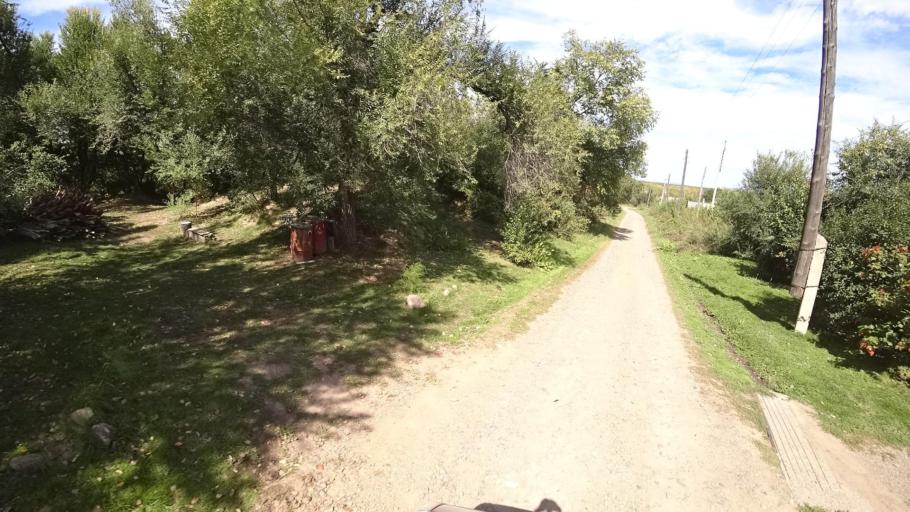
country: RU
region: Primorskiy
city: Yakovlevka
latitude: 44.4339
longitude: 133.5590
